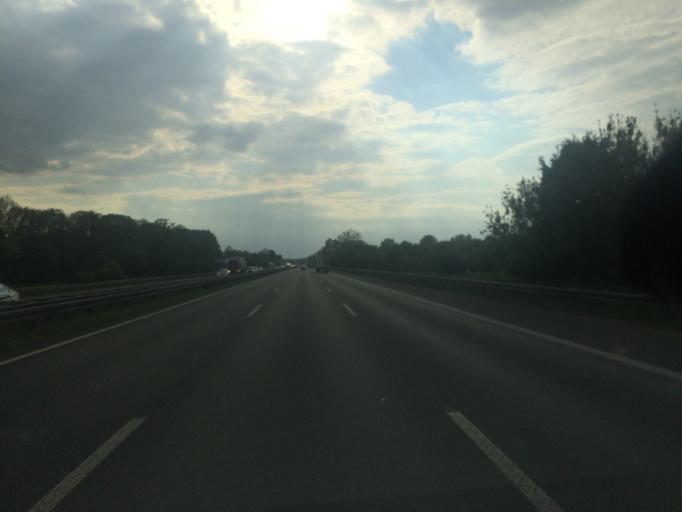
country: DE
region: North Rhine-Westphalia
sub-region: Regierungsbezirk Detmold
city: Guetersloh
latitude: 51.8715
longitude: 8.3997
